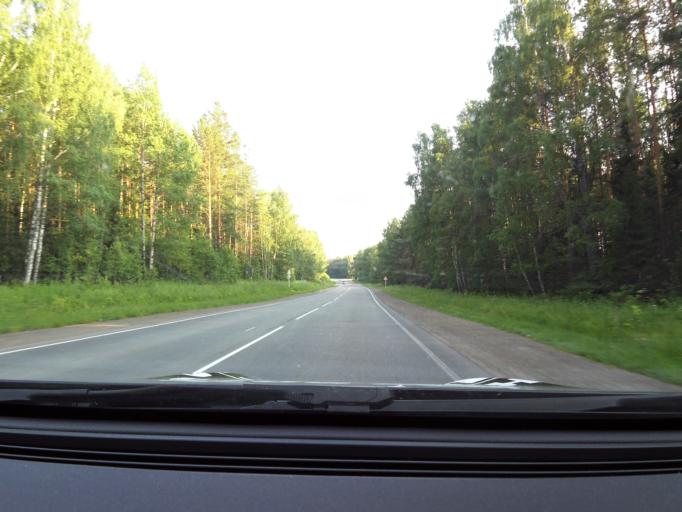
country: RU
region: Sverdlovsk
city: Nizhniye Sergi
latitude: 56.5760
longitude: 59.2133
